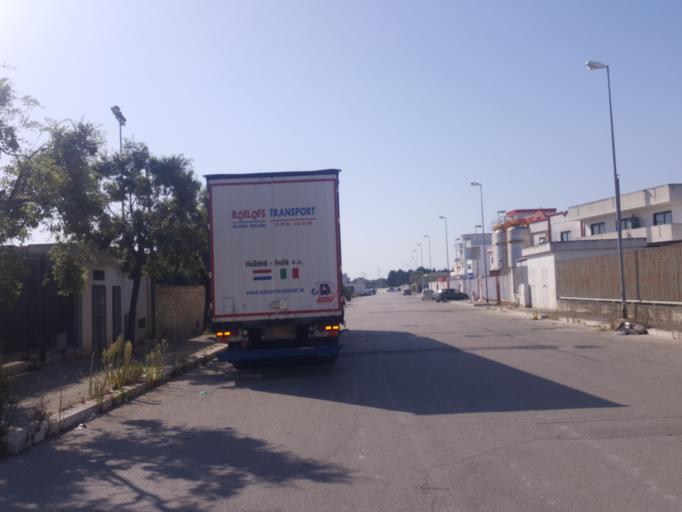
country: IT
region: Apulia
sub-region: Provincia di Barletta - Andria - Trani
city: Barletta
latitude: 41.3103
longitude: 16.3031
